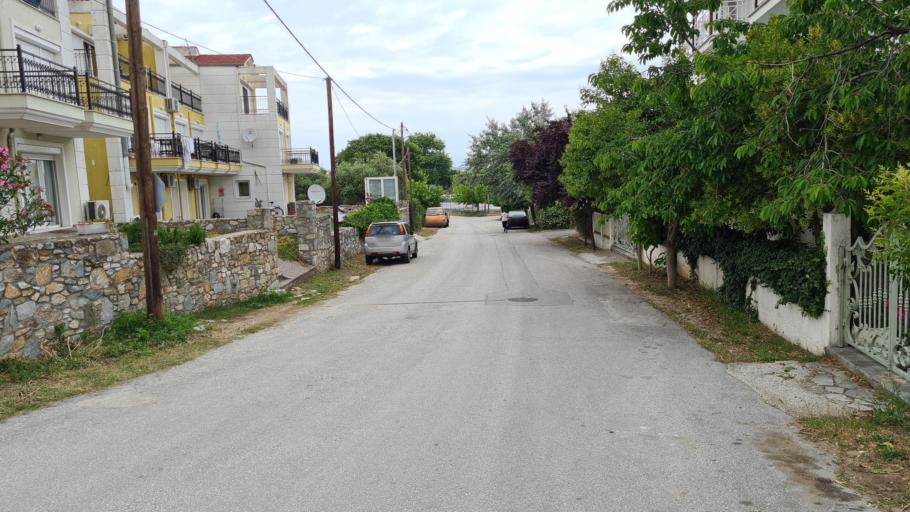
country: GR
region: East Macedonia and Thrace
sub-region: Nomos Kavalas
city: Thasos
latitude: 40.7757
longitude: 24.7014
